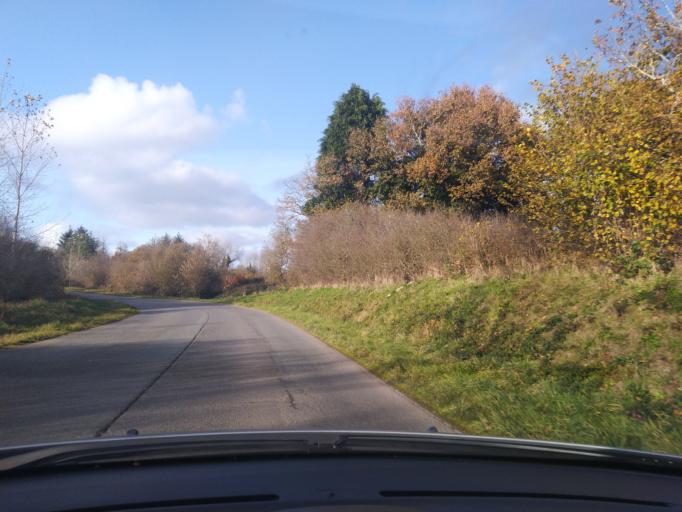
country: FR
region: Brittany
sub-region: Departement du Finistere
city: Guerlesquin
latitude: 48.5208
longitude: -3.5861
